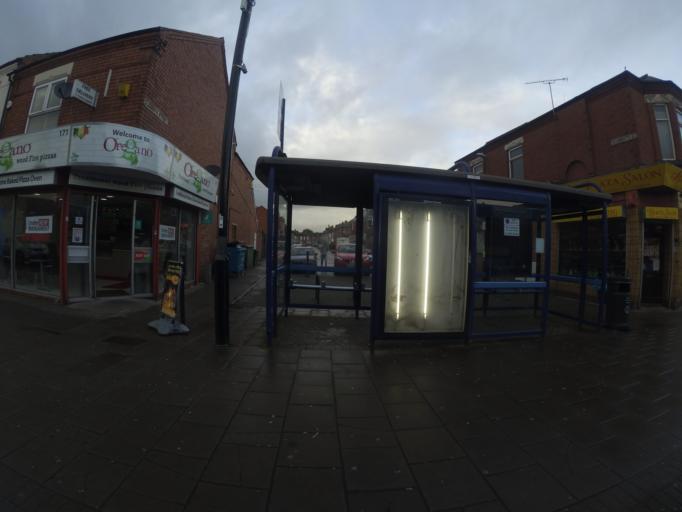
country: GB
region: England
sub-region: Coventry
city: Coventry
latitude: 52.4107
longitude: -1.4848
